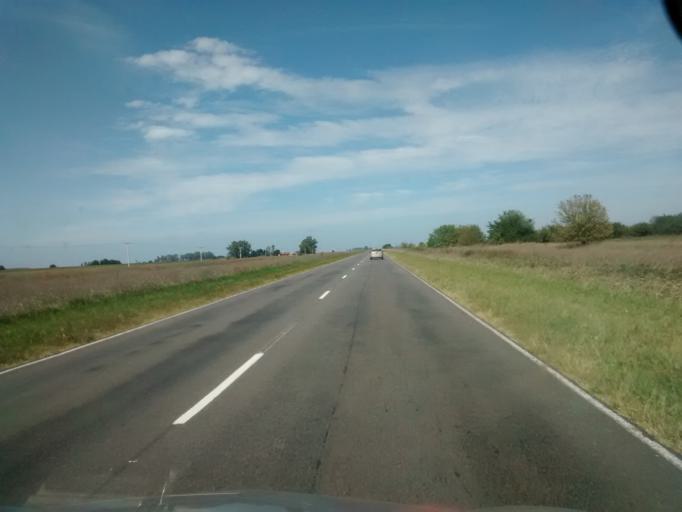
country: AR
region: Buenos Aires
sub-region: Partido de Ayacucho
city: Ayacucho
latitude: -36.6549
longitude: -58.5739
